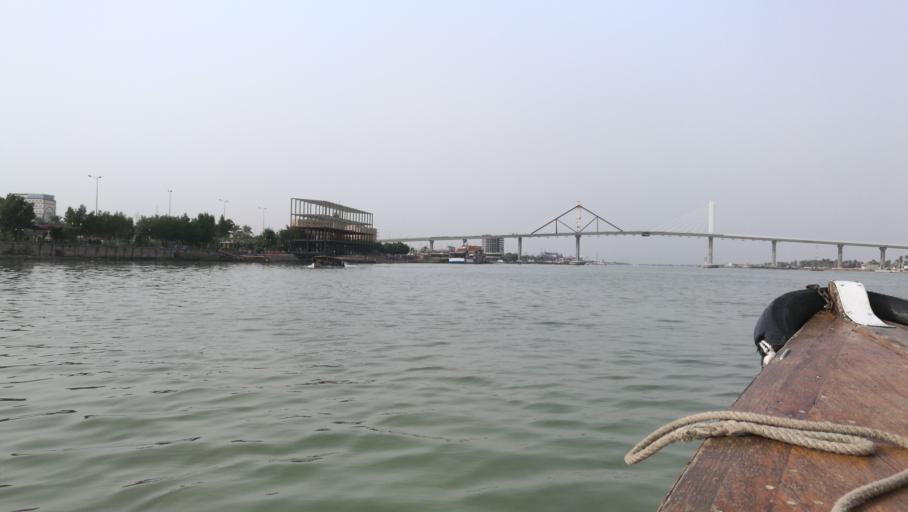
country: IQ
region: Basra Governorate
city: Al Basrah al Qadimah
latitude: 30.5043
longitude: 47.8562
